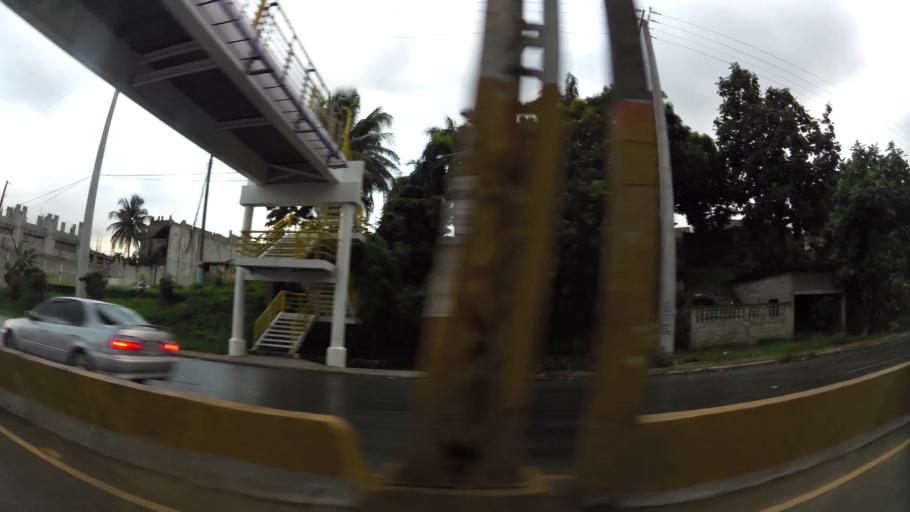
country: DO
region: Santo Domingo
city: Santo Domingo Oeste
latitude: 18.5669
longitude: -70.0876
